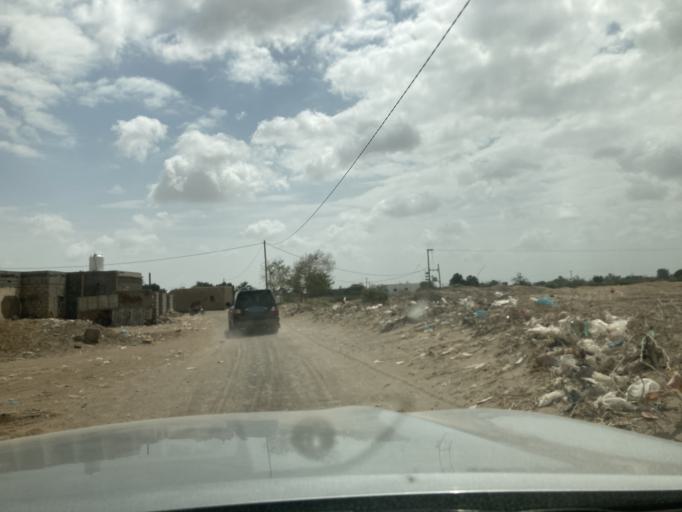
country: YE
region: Lahij
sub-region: Al  Hawtah
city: Lahij
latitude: 13.0183
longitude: 45.0030
